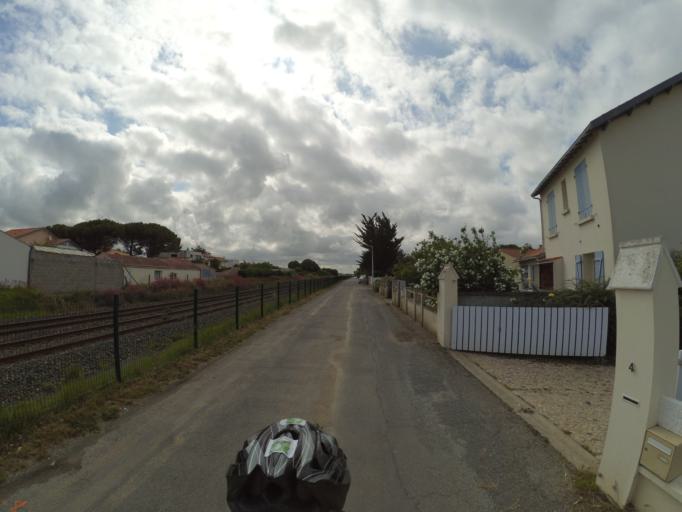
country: FR
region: Poitou-Charentes
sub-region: Departement de la Charente-Maritime
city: Angoulins
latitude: 46.0988
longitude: -1.1074
